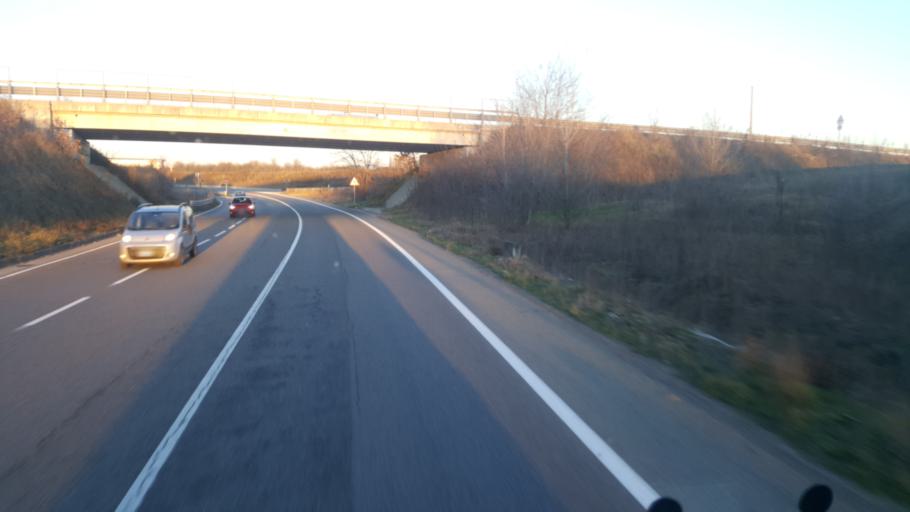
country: IT
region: Emilia-Romagna
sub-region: Provincia di Modena
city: Vignola
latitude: 44.5069
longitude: 11.0226
